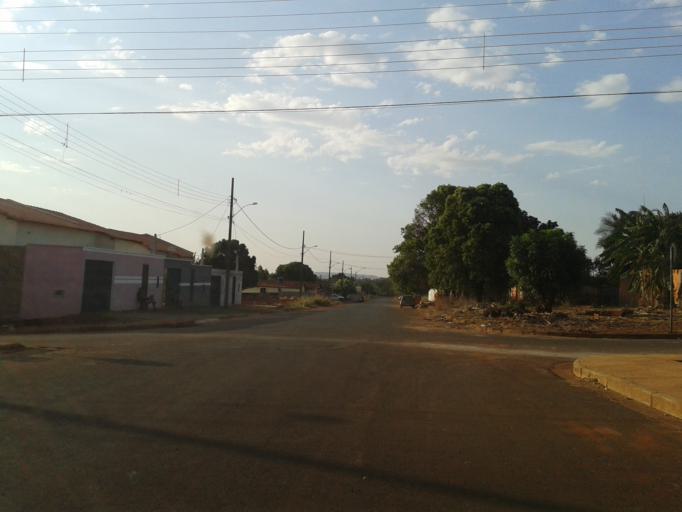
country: BR
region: Minas Gerais
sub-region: Ituiutaba
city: Ituiutaba
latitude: -18.9942
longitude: -49.4377
